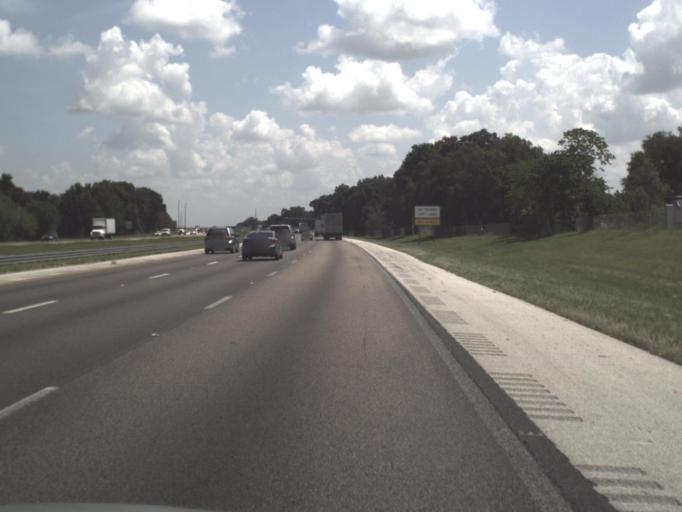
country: US
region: Florida
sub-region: Hillsborough County
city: Seffner
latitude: 28.0087
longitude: -82.2876
